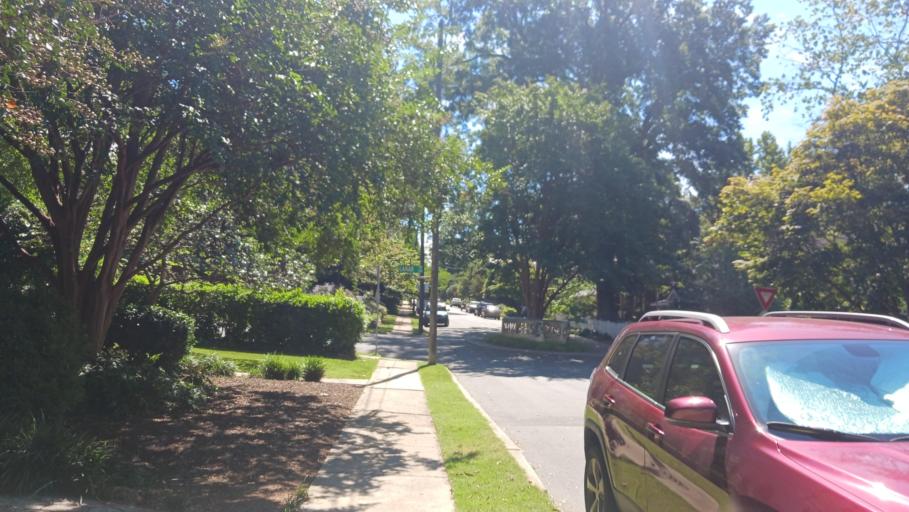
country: US
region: North Carolina
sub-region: Mecklenburg County
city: Charlotte
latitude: 35.2161
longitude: -80.8202
